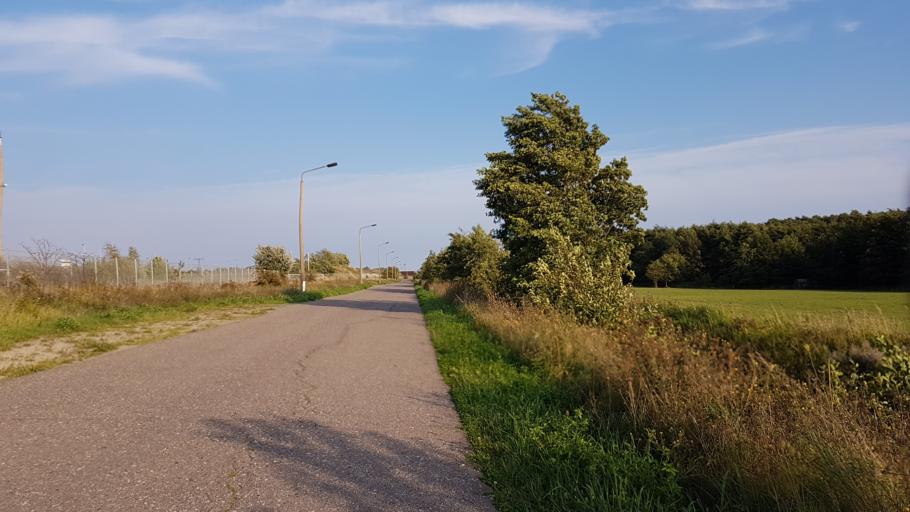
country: DE
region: Mecklenburg-Vorpommern
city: Sagard
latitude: 54.4933
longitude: 13.5617
